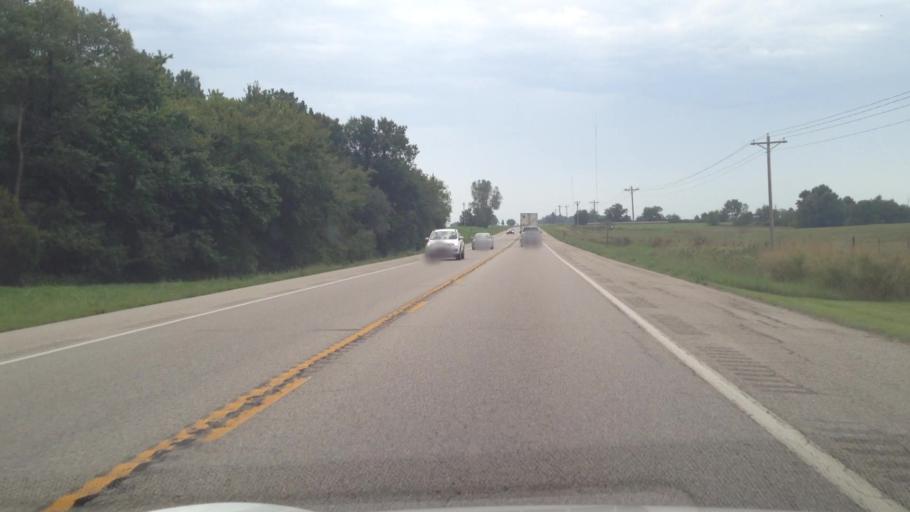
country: US
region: Missouri
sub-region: Jasper County
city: Carl Junction
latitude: 37.2476
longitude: -94.7051
